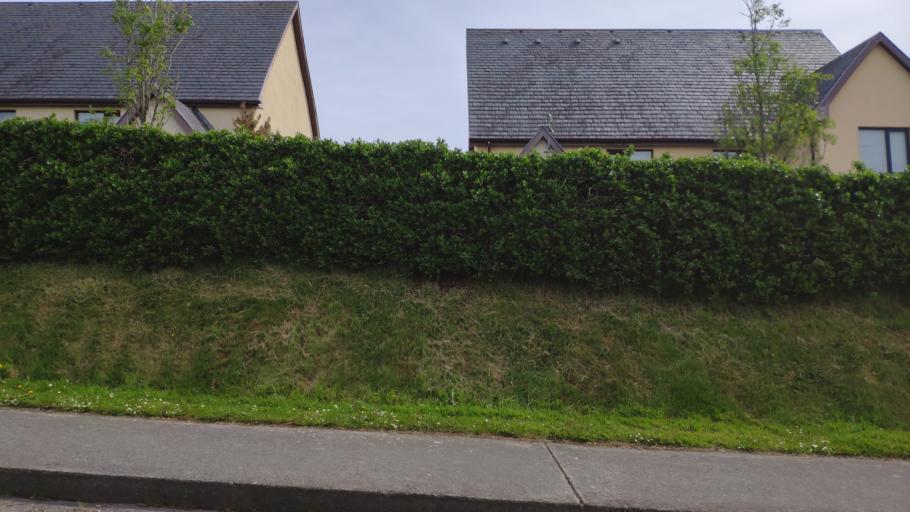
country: IE
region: Munster
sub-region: County Cork
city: Blarney
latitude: 51.9798
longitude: -8.5139
